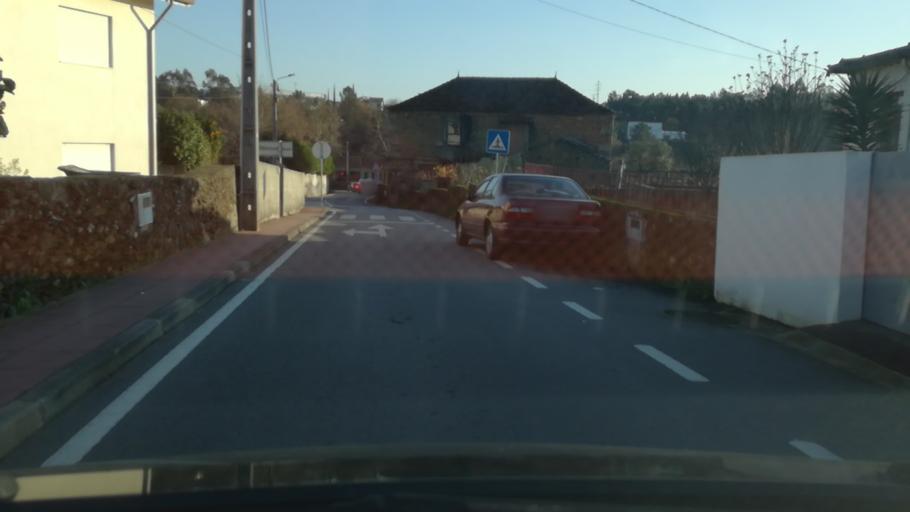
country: PT
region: Braga
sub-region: Vila Nova de Famalicao
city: Ferreiros
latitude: 41.3503
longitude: -8.5212
